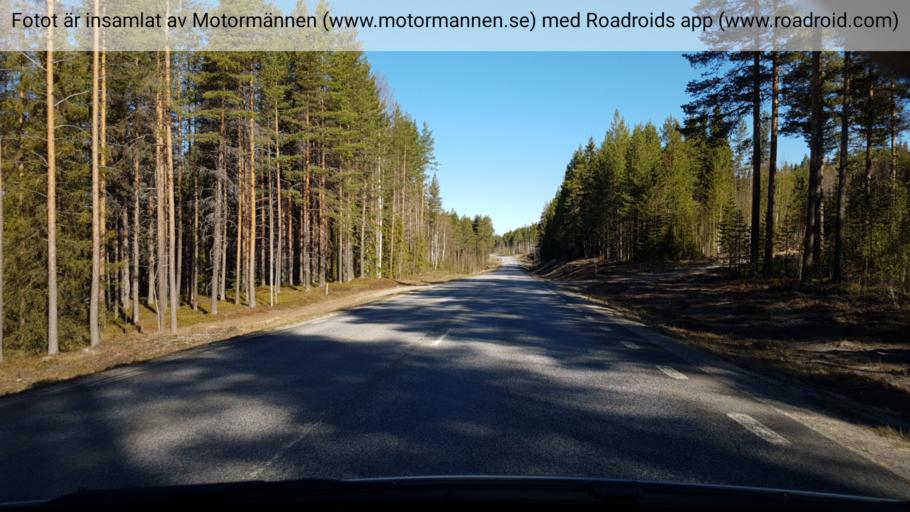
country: SE
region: Vaesterbotten
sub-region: Lycksele Kommun
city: Lycksele
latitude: 64.5418
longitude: 18.7508
